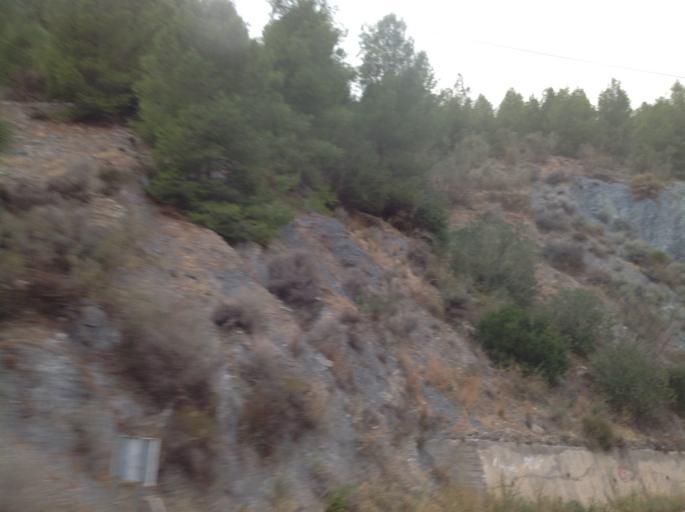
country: ES
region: Andalusia
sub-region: Provincia de Malaga
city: Carratraca
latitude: 36.9071
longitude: -4.7644
